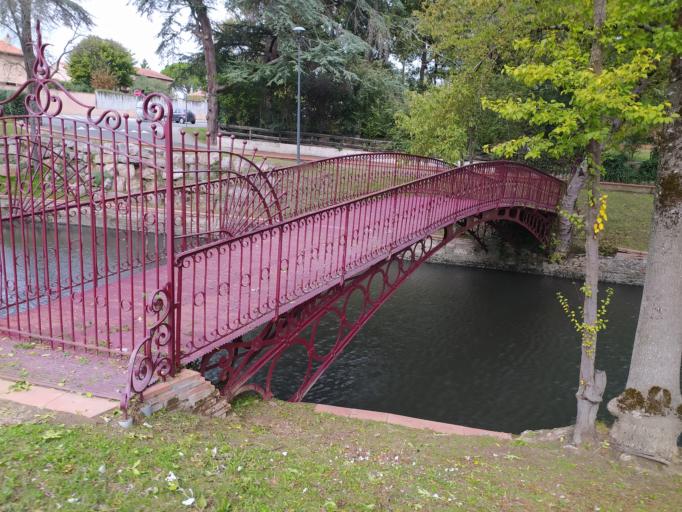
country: FR
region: Midi-Pyrenees
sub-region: Departement de la Haute-Garonne
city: Tournefeuille
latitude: 43.5981
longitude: 1.3296
